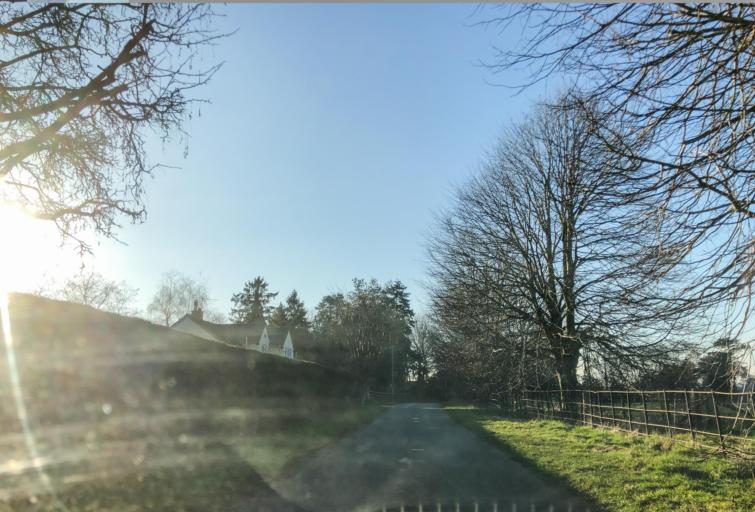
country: GB
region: England
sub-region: Warwickshire
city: Warwick
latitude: 52.2479
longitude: -1.5933
